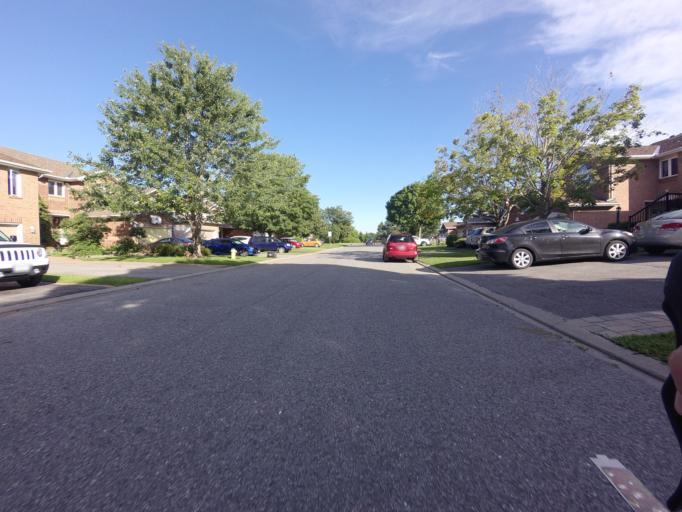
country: CA
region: Ontario
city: Bells Corners
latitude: 45.2933
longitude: -75.7374
